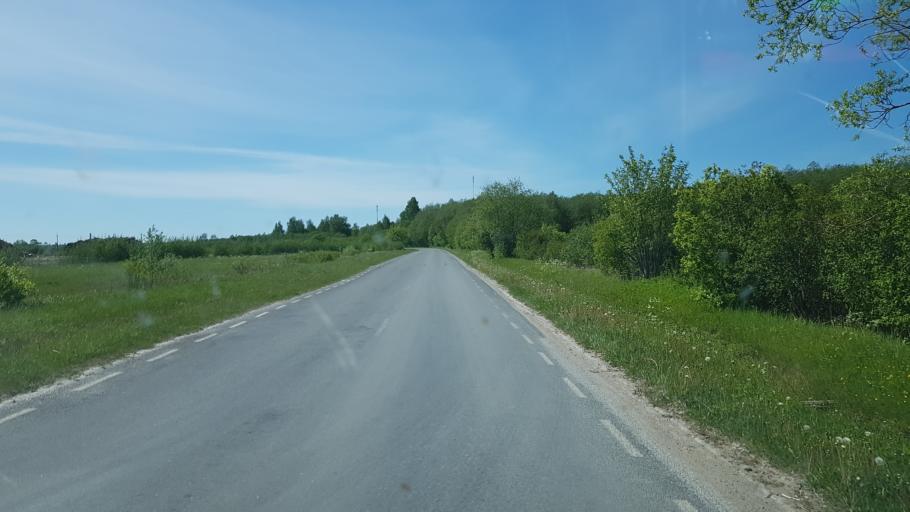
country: EE
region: Saare
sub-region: Kuressaare linn
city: Kuressaare
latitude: 58.2808
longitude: 22.5035
